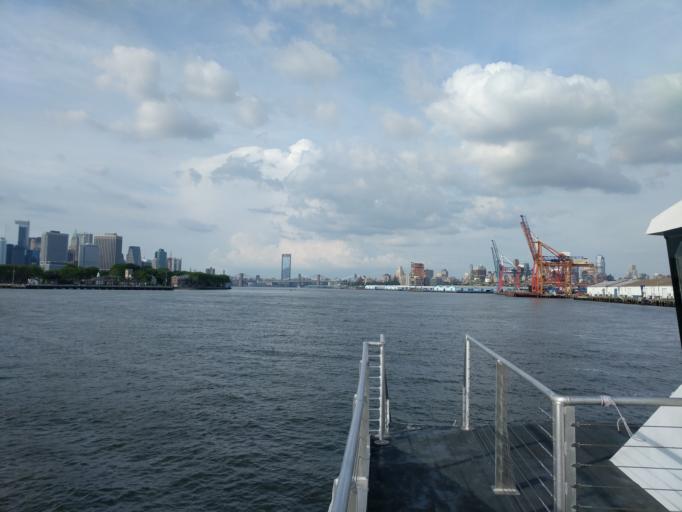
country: US
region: New York
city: New York City
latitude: 40.6820
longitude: -74.0175
